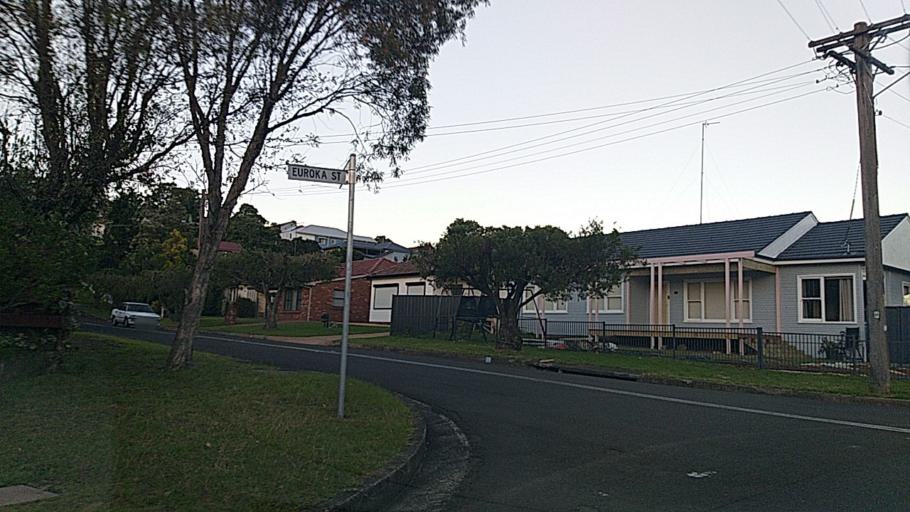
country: AU
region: New South Wales
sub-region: Wollongong
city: West Wollongong
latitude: -34.4223
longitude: 150.8597
